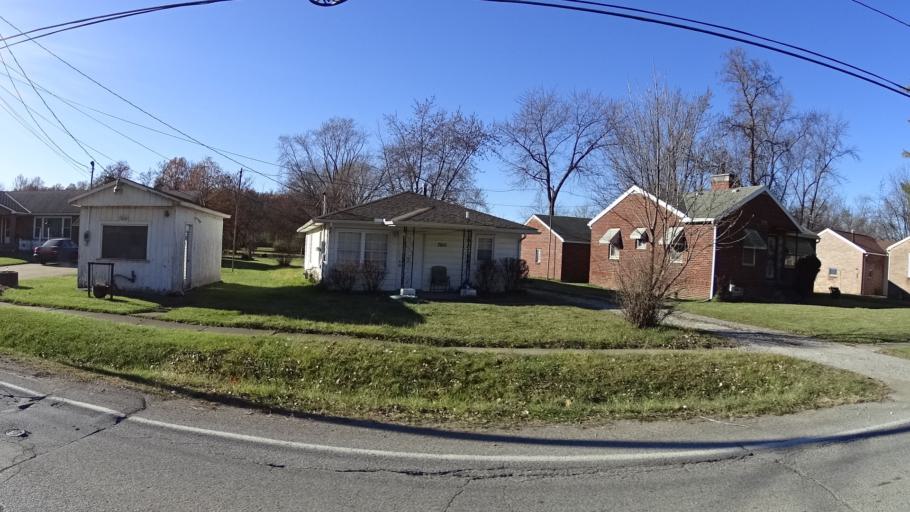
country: US
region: Ohio
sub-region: Lorain County
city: Elyria
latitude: 41.3509
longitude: -82.1203
